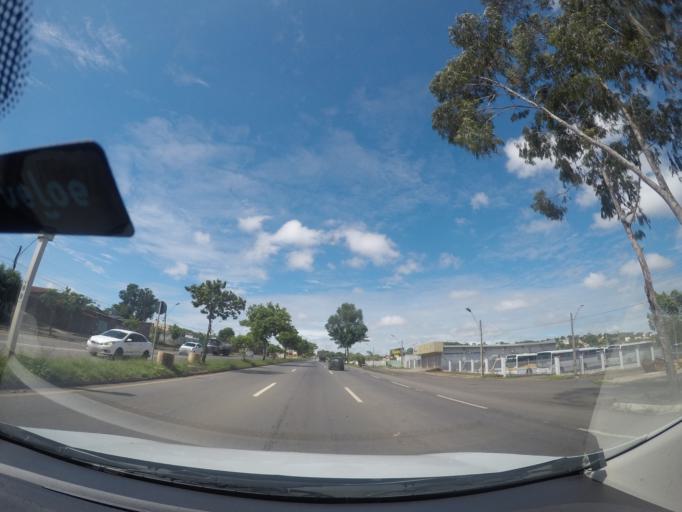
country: BR
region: Goias
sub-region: Goiania
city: Goiania
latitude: -16.6381
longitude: -49.2844
